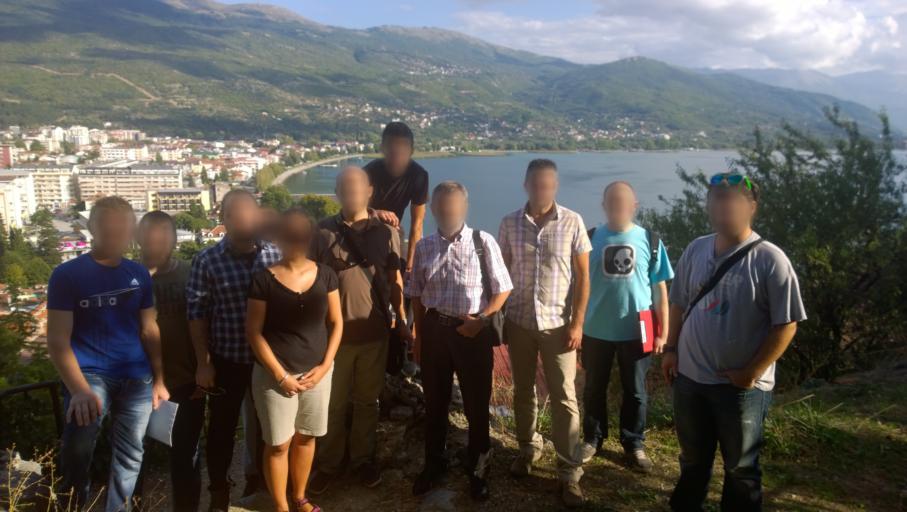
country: MK
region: Ohrid
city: Ohrid
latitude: 41.1141
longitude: 20.7974
